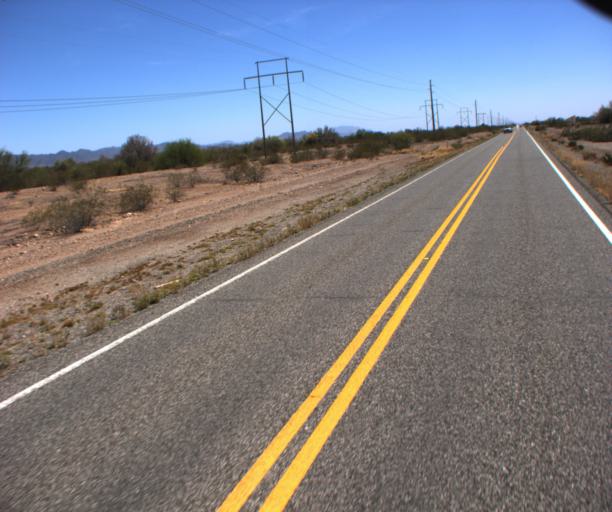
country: US
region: Arizona
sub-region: La Paz County
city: Quartzsite
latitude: 33.7582
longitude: -114.2170
